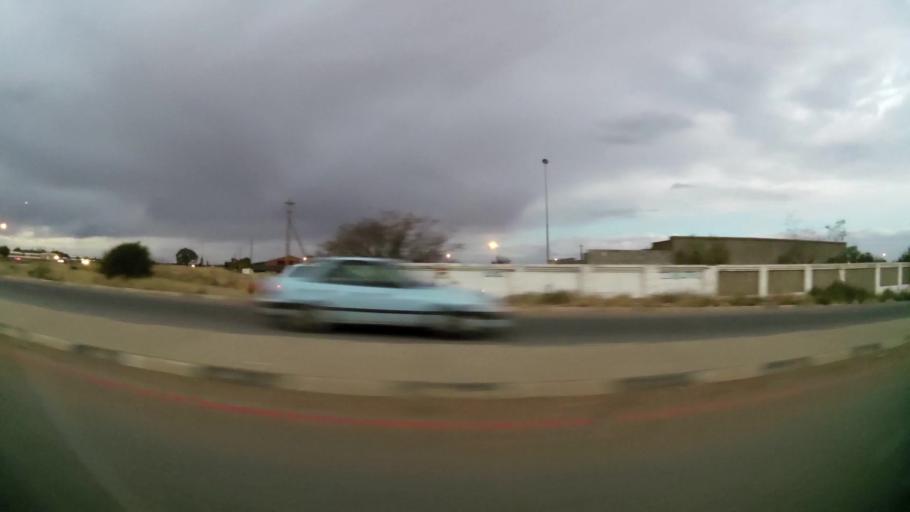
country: ZA
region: Orange Free State
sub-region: Lejweleputswa District Municipality
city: Welkom
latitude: -27.9561
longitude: 26.7855
